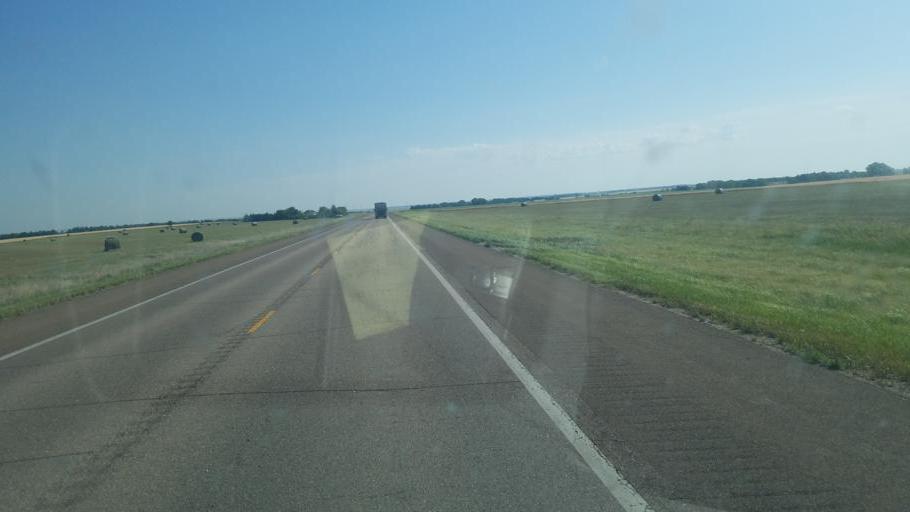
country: US
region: Kansas
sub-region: Barton County
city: Great Bend
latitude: 38.3921
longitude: -98.6757
